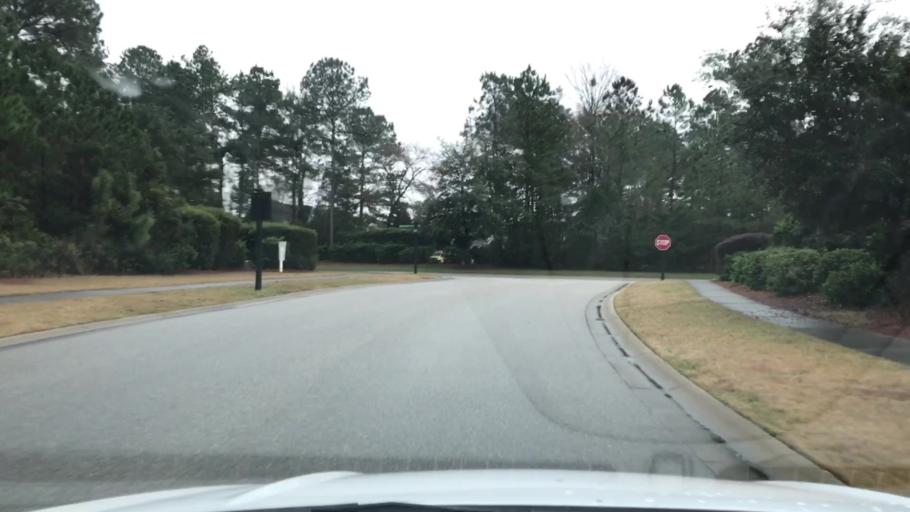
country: US
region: South Carolina
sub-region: Horry County
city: Myrtle Beach
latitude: 33.7454
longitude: -78.9030
